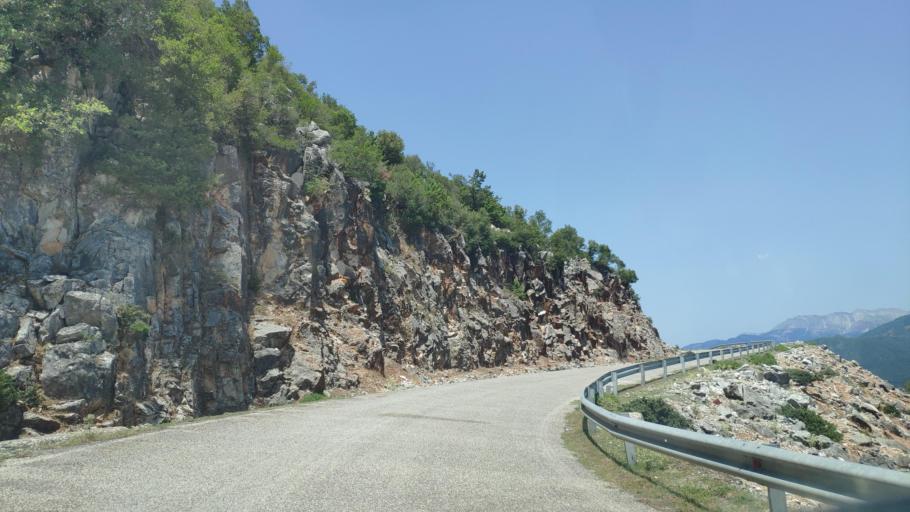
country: GR
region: Thessaly
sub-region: Nomos Kardhitsas
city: Anthiro
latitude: 39.1219
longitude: 21.4009
